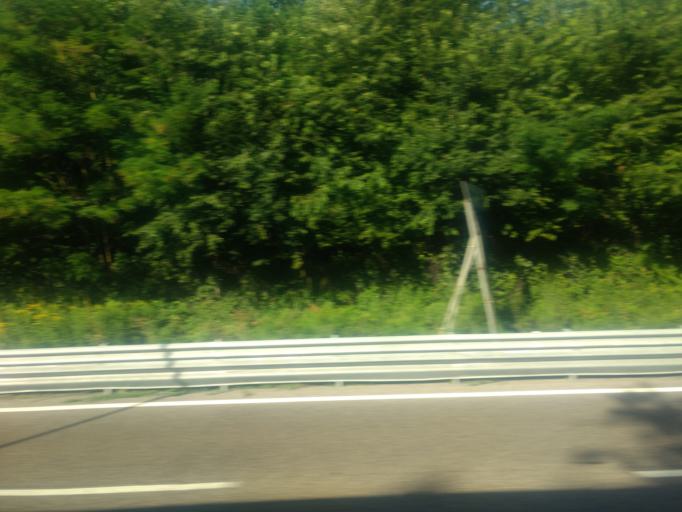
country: IT
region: Lombardy
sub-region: Provincia di Varese
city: Cardano al Campo
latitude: 45.6475
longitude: 8.7474
